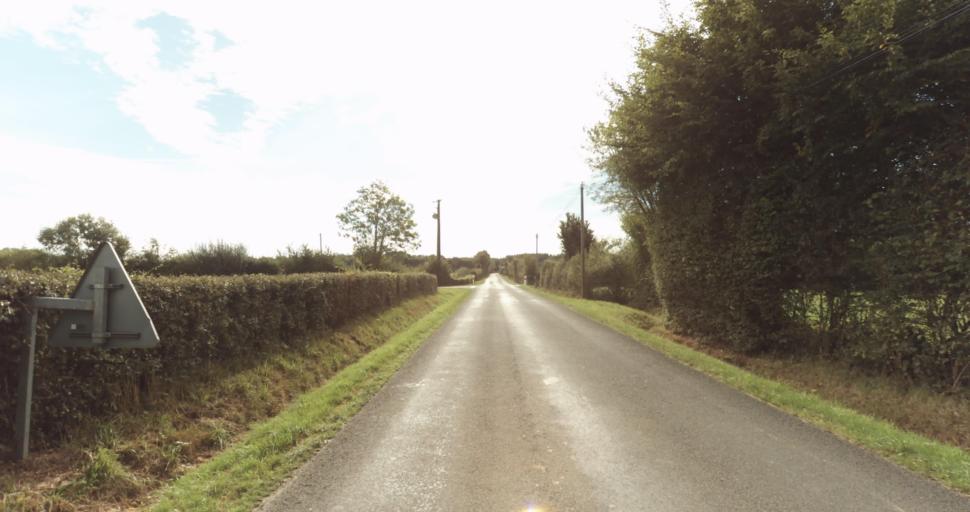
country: FR
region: Lower Normandy
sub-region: Departement de l'Orne
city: Gace
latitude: 48.8102
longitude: 0.2441
